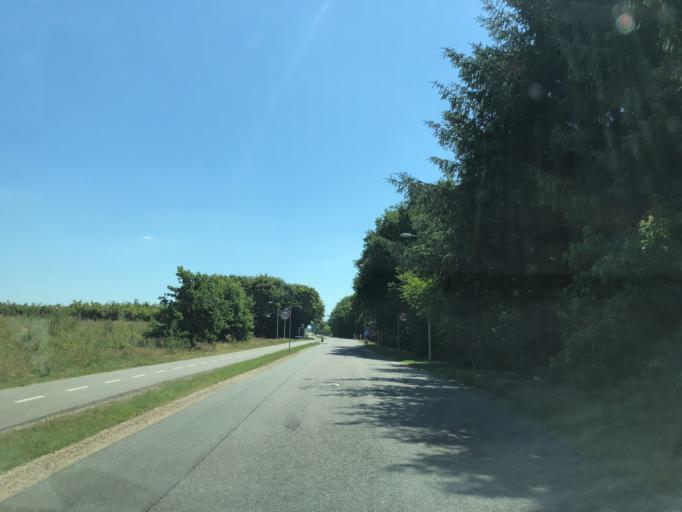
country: DK
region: Central Jutland
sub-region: Holstebro Kommune
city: Holstebro
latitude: 56.3433
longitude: 8.6698
